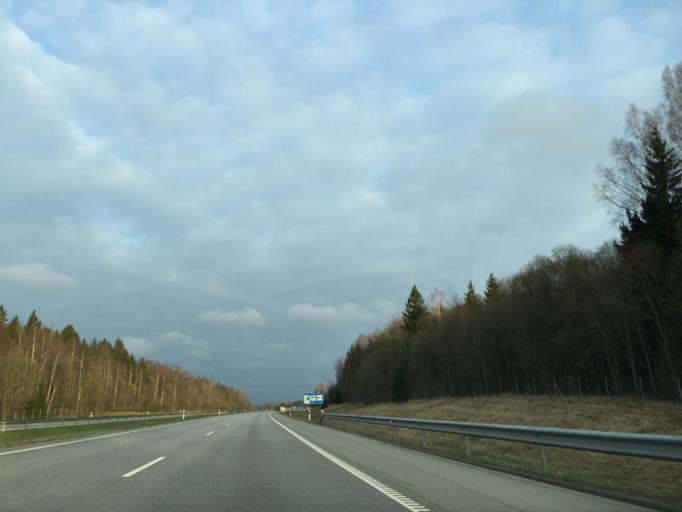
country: LT
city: Rietavas
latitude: 55.6920
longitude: 21.6753
